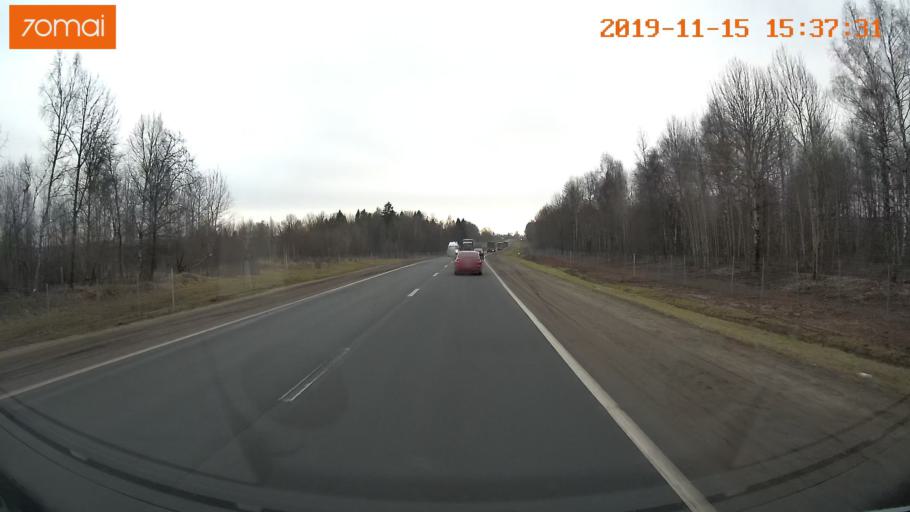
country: RU
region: Jaroslavl
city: Danilov
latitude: 58.0387
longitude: 40.0881
